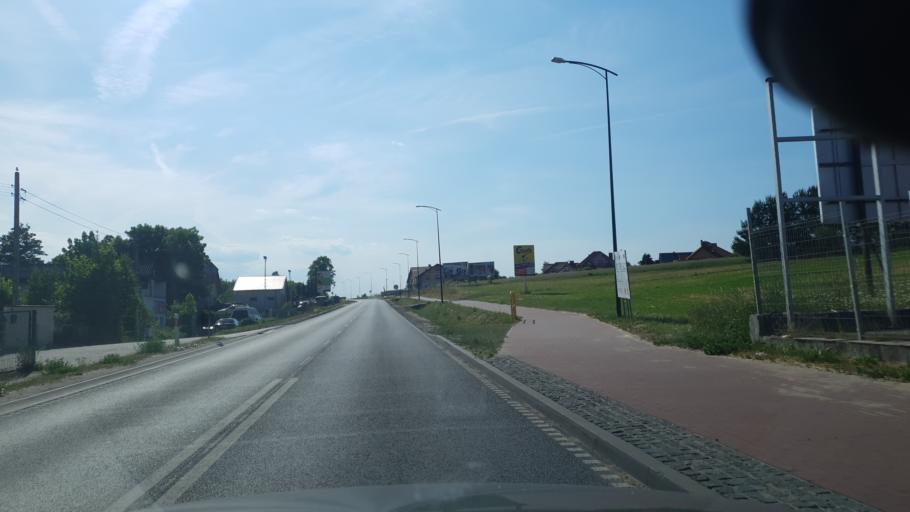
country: PL
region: Pomeranian Voivodeship
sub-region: Powiat kartuski
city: Chwaszczyno
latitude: 54.4426
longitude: 18.4421
